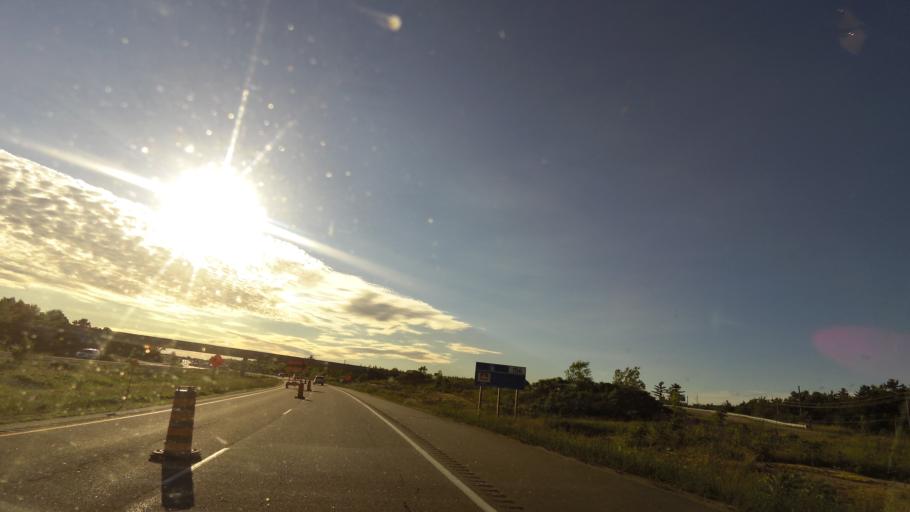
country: CA
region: Ontario
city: Midland
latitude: 44.7969
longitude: -79.7103
